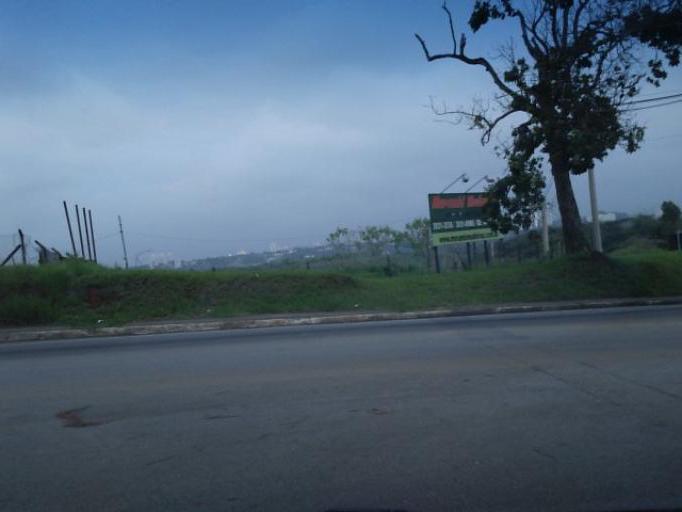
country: BR
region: Sao Paulo
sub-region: Sao Jose Dos Campos
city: Sao Jose dos Campos
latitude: -23.2480
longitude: -45.8618
